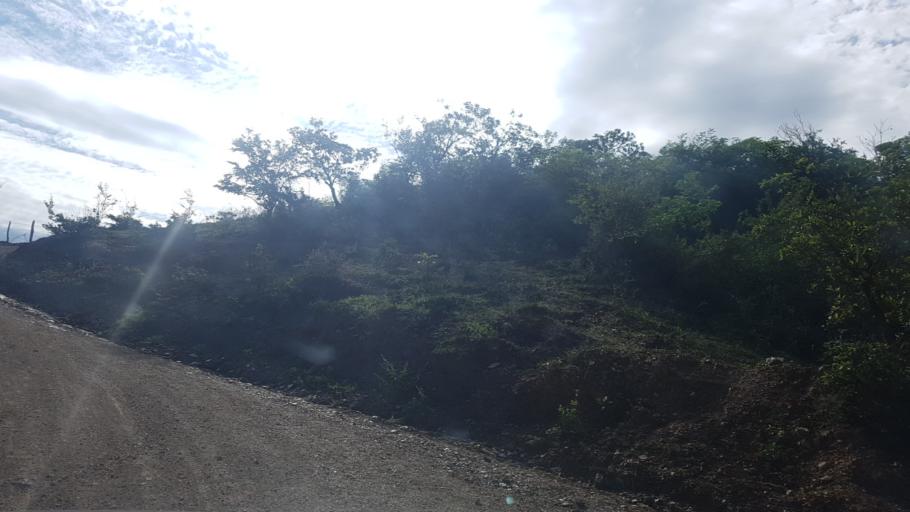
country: NI
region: Nueva Segovia
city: Ocotal
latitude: 13.6057
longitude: -86.4451
